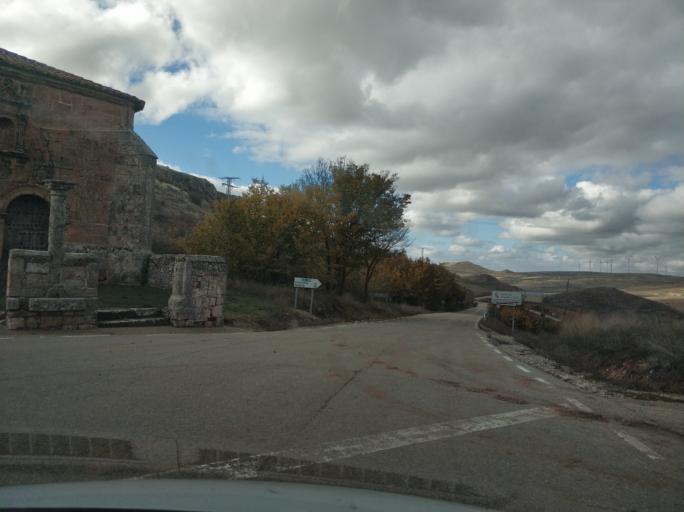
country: ES
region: Castille and Leon
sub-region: Provincia de Soria
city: Medinaceli
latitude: 41.1690
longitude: -2.4380
